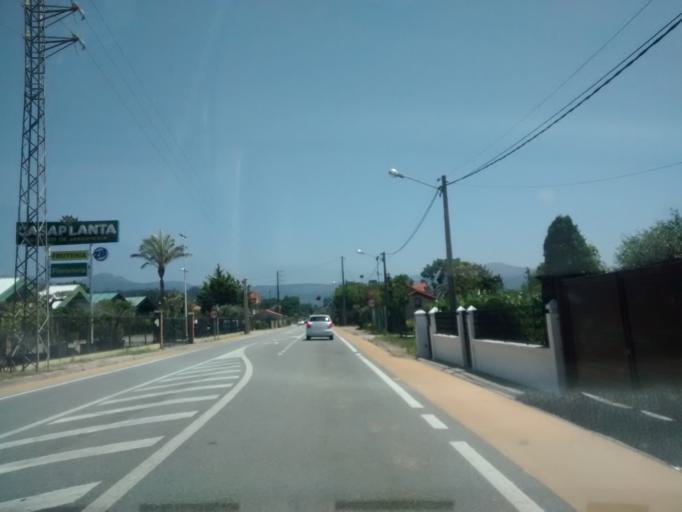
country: ES
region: Galicia
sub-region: Provincia de Pontevedra
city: Nigran
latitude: 42.1146
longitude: -8.8008
